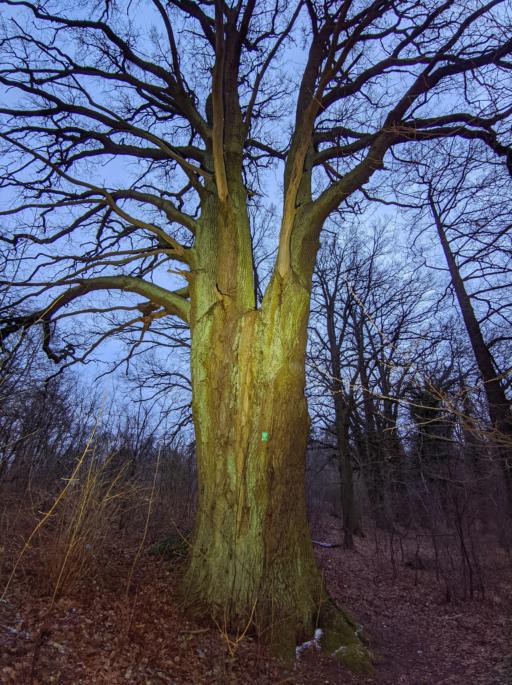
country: PL
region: Lubusz
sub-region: Zielona Gora
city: Zielona Gora
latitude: 51.9302
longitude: 15.6101
